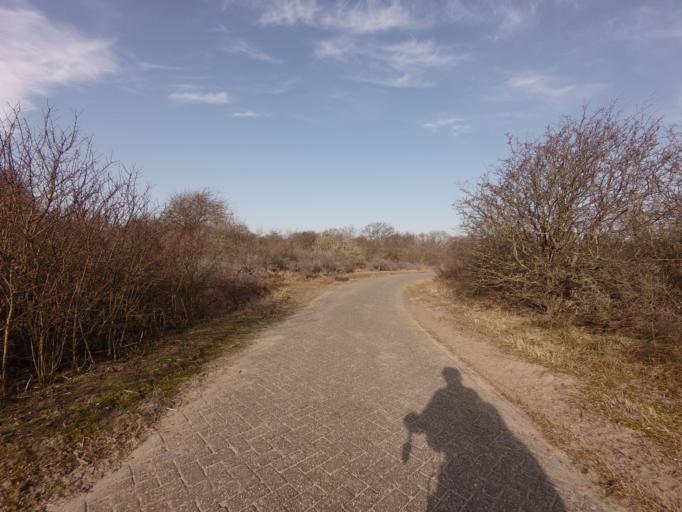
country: NL
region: North Holland
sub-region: Gemeente Zandvoort
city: Zandvoort
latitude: 52.3701
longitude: 4.5632
